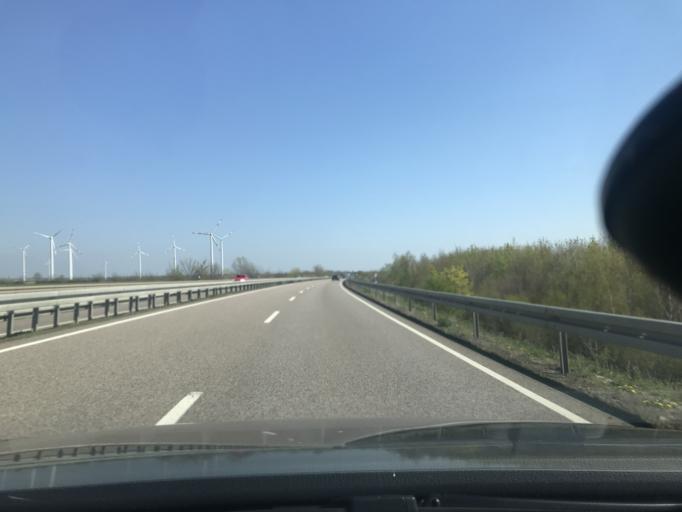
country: DE
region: Saxony-Anhalt
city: Brehna
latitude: 51.5679
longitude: 12.2073
